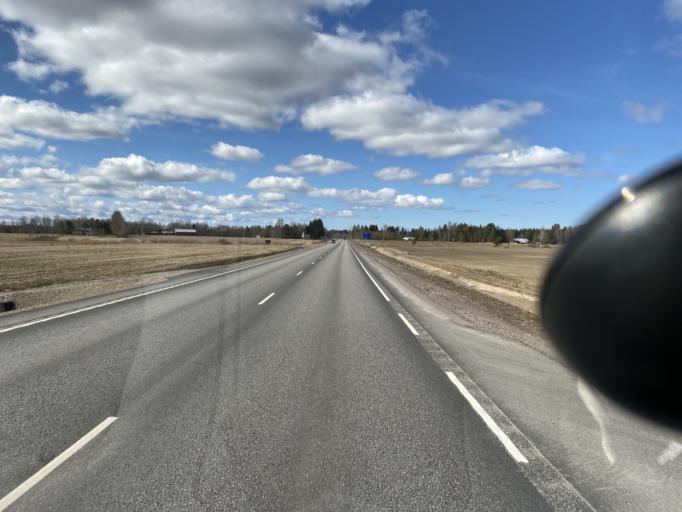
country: FI
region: Satakunta
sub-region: Rauma
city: Koeylioe
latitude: 61.1628
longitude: 22.3266
